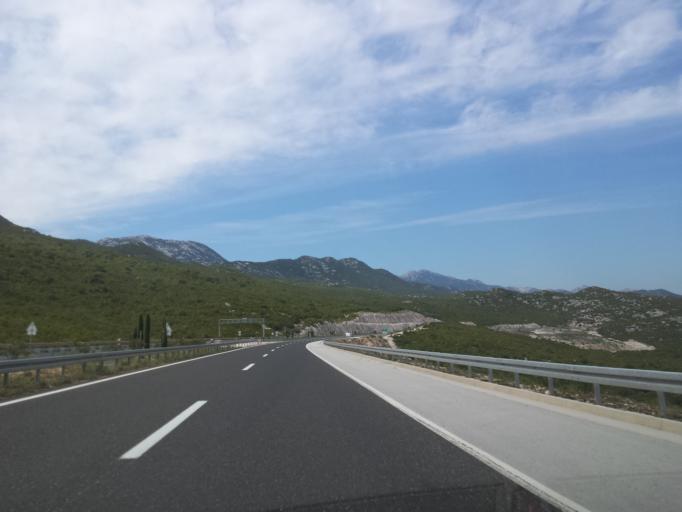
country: HR
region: Splitsko-Dalmatinska
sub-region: Grad Omis
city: Omis
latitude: 43.4792
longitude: 16.8175
